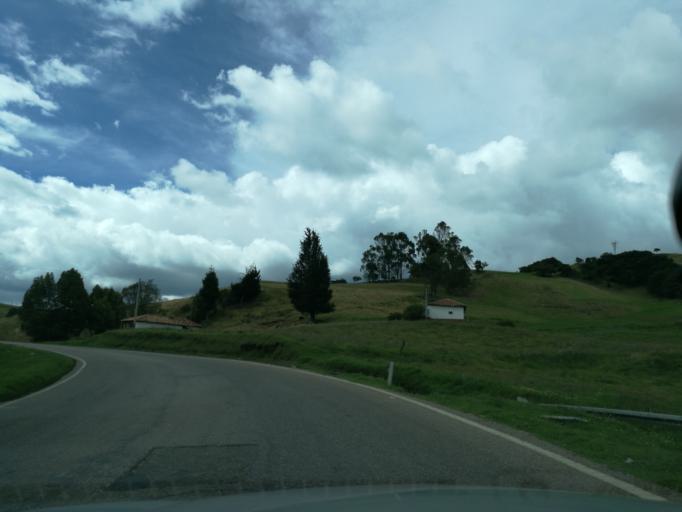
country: CO
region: Boyaca
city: Combita
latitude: 5.6621
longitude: -73.3580
